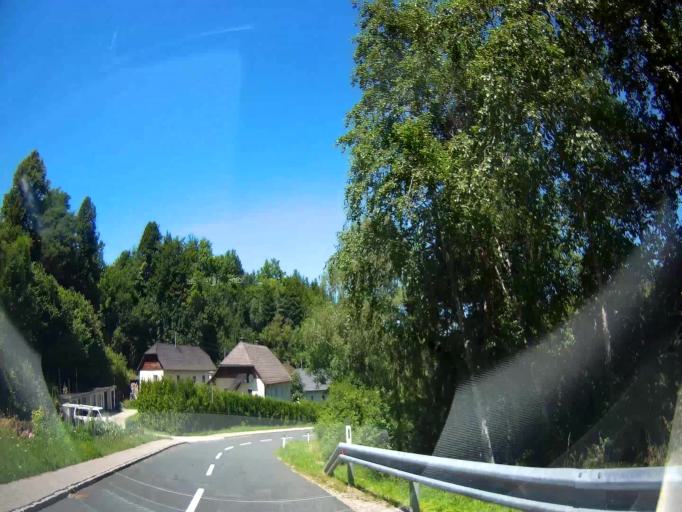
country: AT
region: Carinthia
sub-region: Politischer Bezirk Klagenfurt Land
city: Ferlach
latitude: 46.5078
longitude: 14.2906
